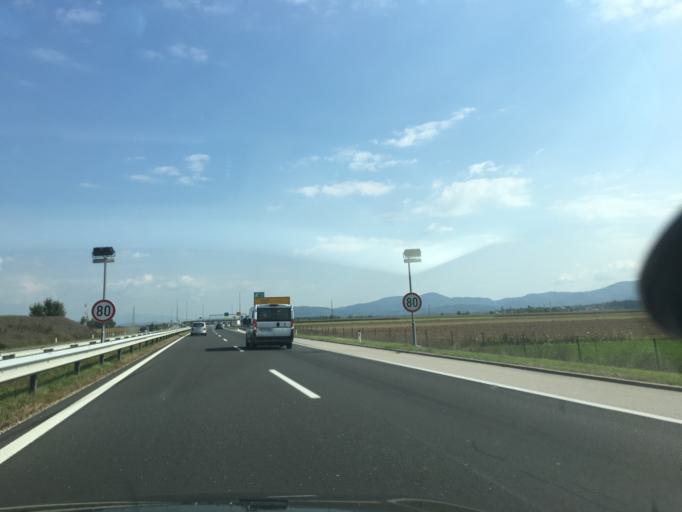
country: SI
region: Krsko
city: Leskovec pri Krskem
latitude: 45.9140
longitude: 15.4583
